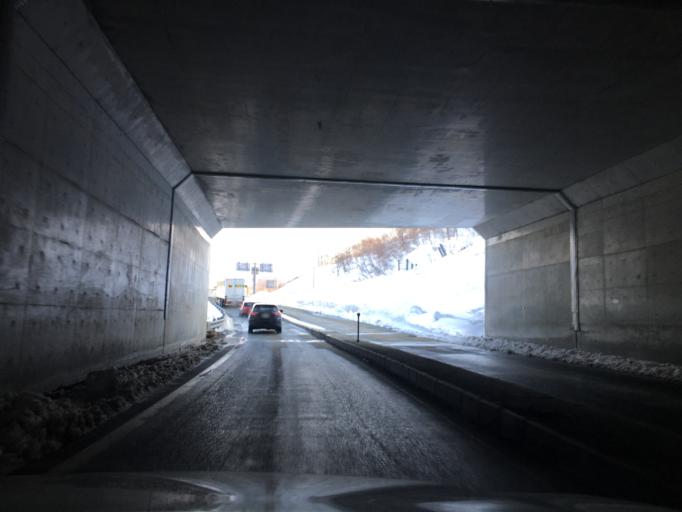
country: JP
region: Yamagata
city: Sagae
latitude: 38.4557
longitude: 139.9921
